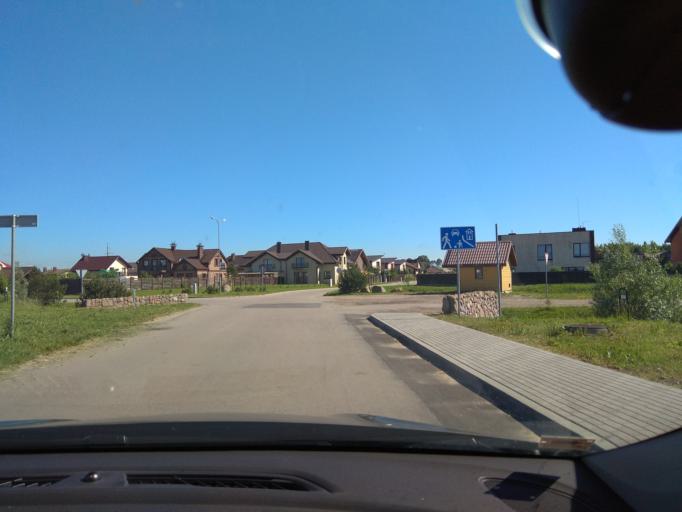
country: LT
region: Klaipedos apskritis
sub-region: Klaipeda
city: Klaipeda
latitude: 55.7495
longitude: 21.1786
